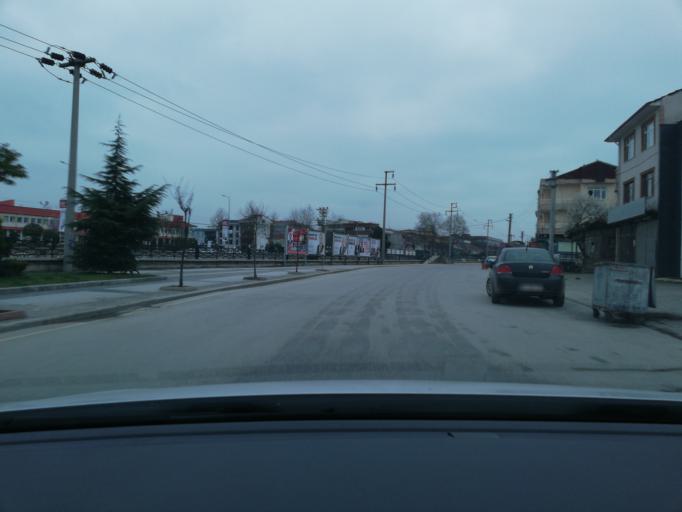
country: TR
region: Duzce
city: Duzce
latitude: 40.8373
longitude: 31.1539
